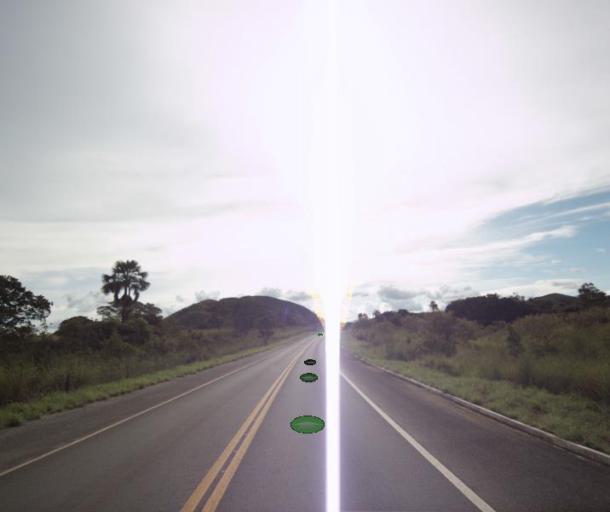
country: BR
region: Goias
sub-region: Barro Alto
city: Barro Alto
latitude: -15.1210
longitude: -48.7256
